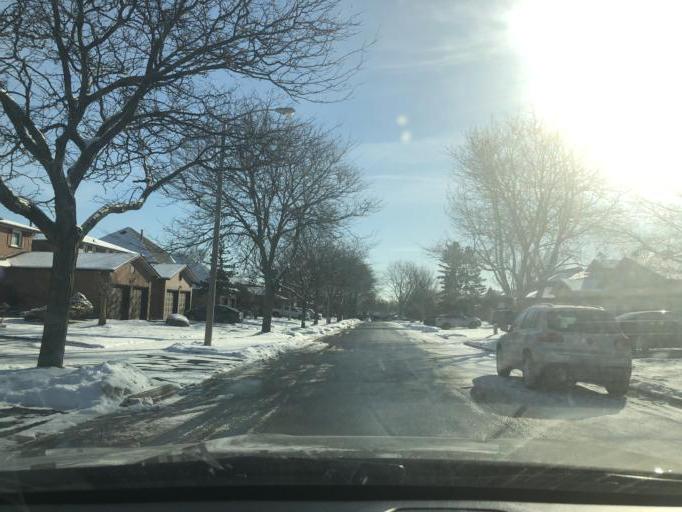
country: CA
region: Ontario
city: Scarborough
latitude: 43.7896
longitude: -79.1533
